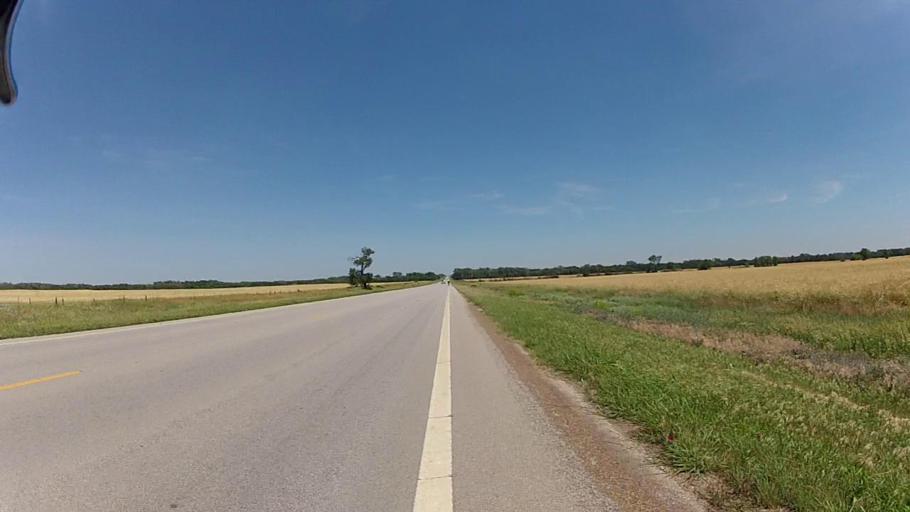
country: US
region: Kansas
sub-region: Harper County
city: Harper
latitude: 37.2384
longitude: -98.1068
